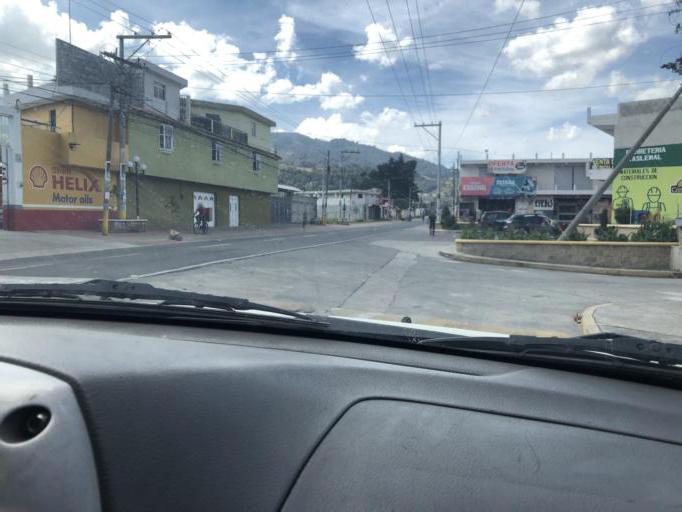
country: GT
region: Quetzaltenango
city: San Mateo
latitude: 14.8634
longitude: -91.5838
